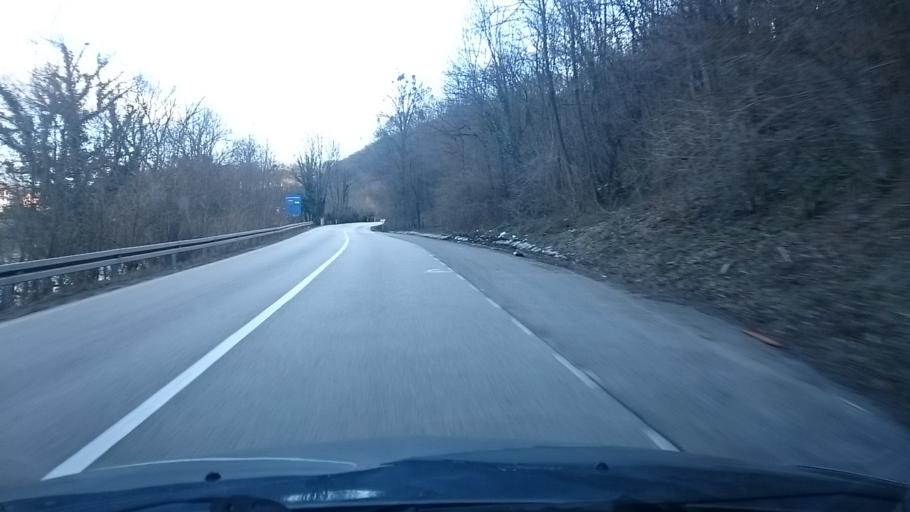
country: BA
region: Republika Srpska
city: Hiseti
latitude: 44.7005
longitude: 17.1851
